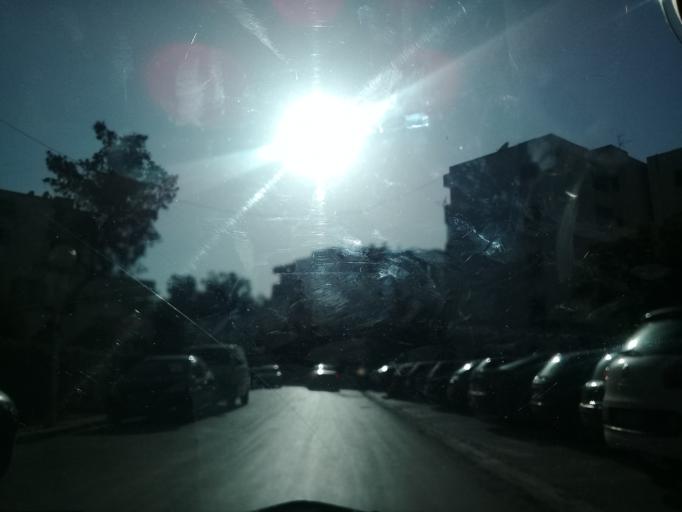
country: TN
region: Ariana
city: Ariana
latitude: 36.8372
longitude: 10.1934
